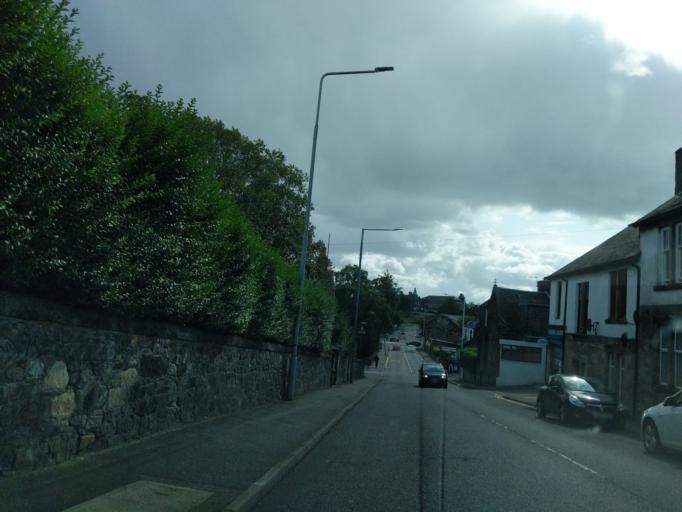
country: GB
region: Scotland
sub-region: Fife
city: Dunfermline
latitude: 56.0756
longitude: -3.4511
